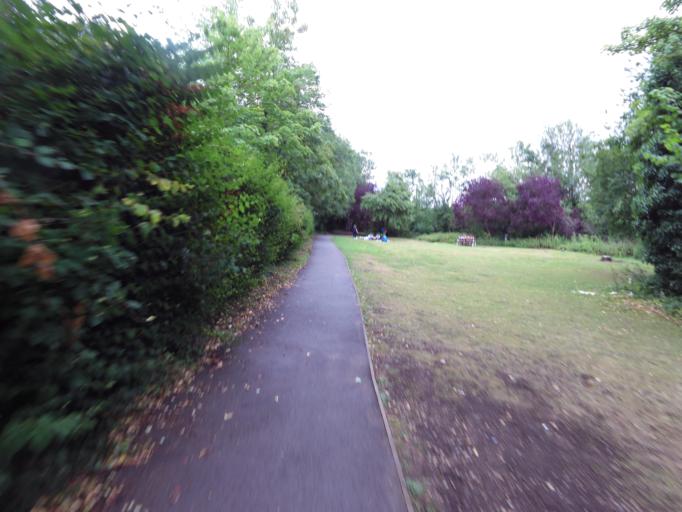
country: GB
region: England
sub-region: Hertfordshire
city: Broxbourne
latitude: 51.7442
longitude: -0.0135
